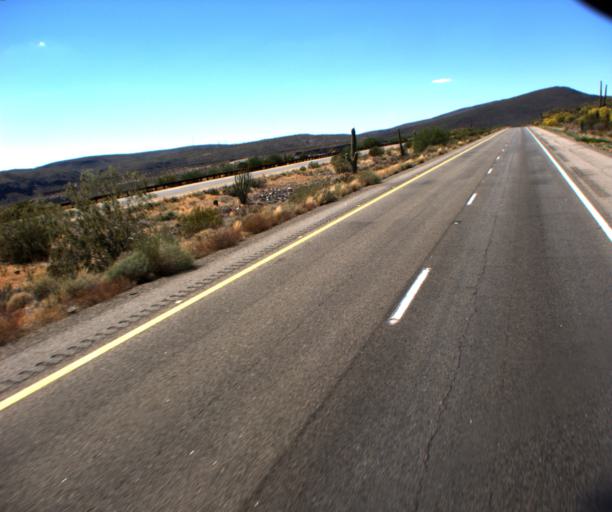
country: US
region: Arizona
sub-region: Yavapai County
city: Bagdad
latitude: 34.5363
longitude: -113.4336
